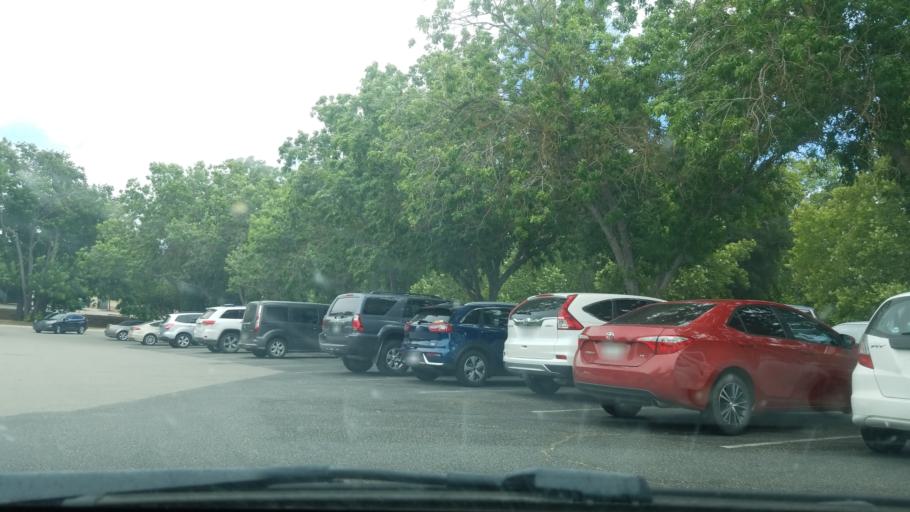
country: US
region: California
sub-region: San Luis Obispo County
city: Atascadero
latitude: 35.4671
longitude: -120.6700
